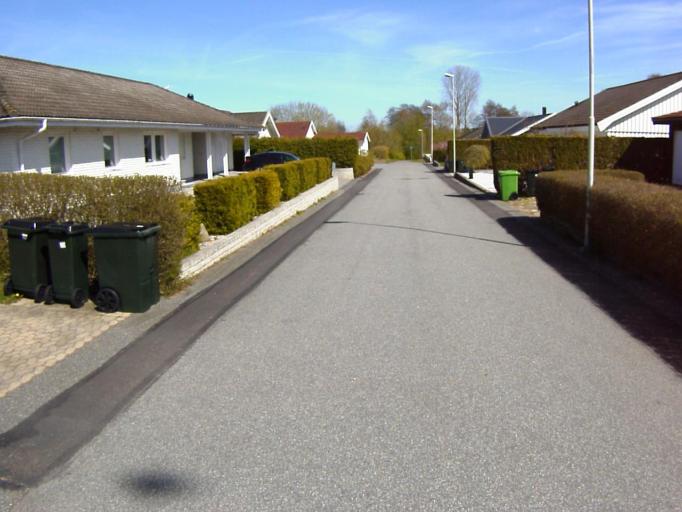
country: SE
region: Skane
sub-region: Kristianstads Kommun
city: Onnestad
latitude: 55.9985
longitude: 14.0694
